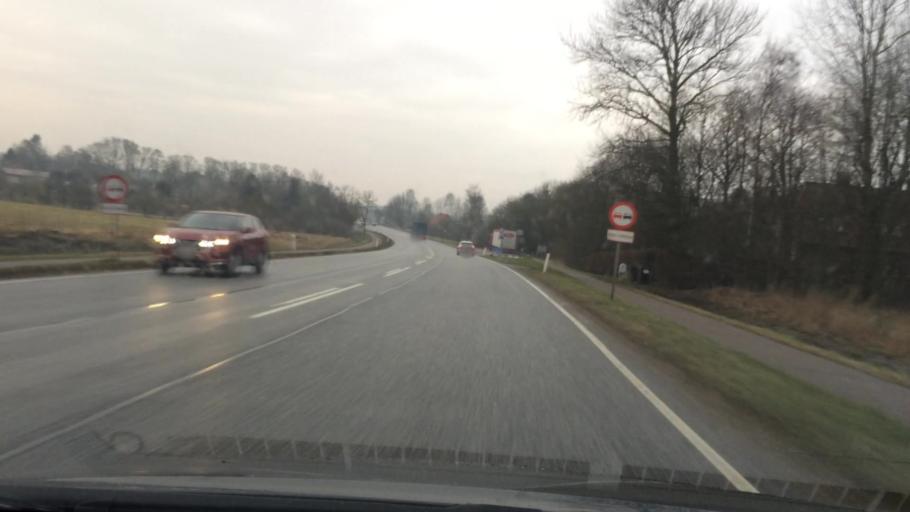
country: DK
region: Central Jutland
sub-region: Horsens Kommune
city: Horsens
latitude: 55.8233
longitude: 9.7932
